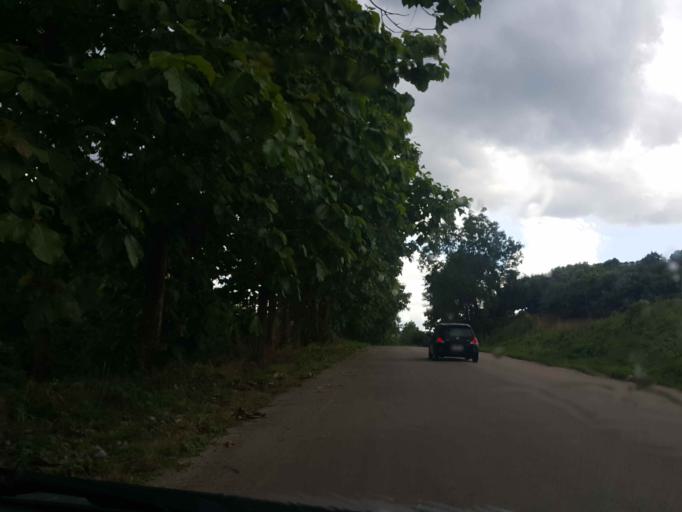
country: TH
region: Phayao
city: Dok Kham Tai
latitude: 18.9862
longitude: 100.0676
